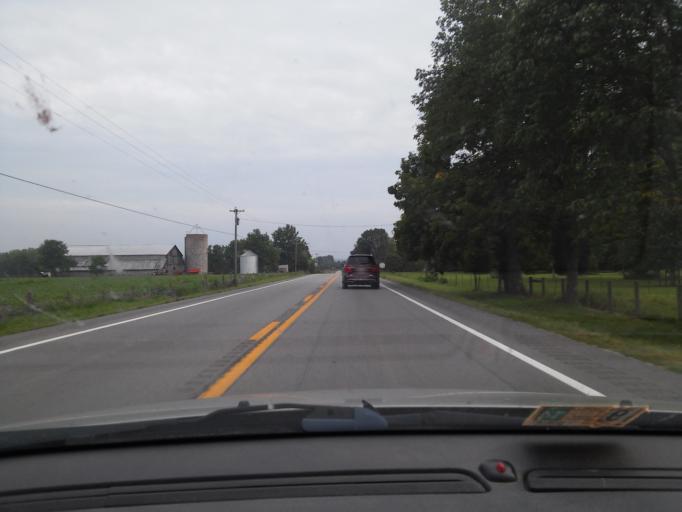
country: US
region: West Virginia
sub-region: Putnam County
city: Buffalo
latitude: 38.6583
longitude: -81.9691
